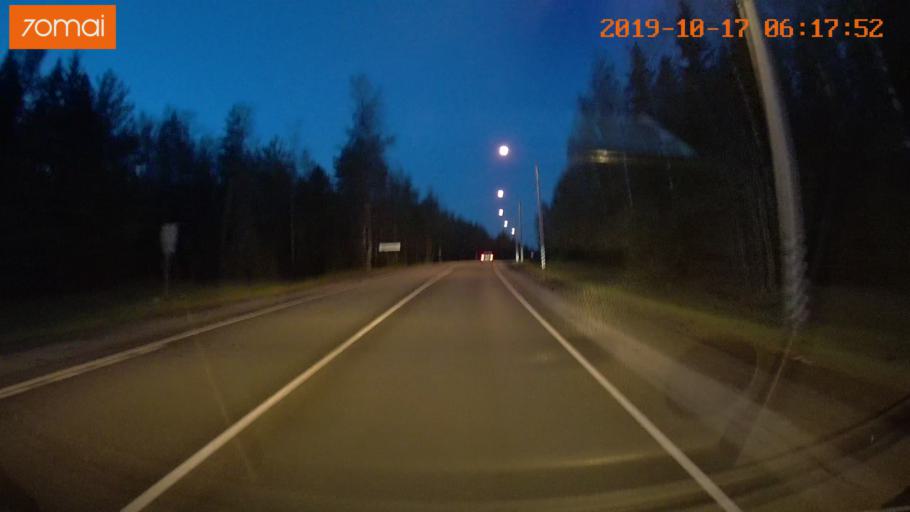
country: RU
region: Ivanovo
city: Lezhnevo
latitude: 56.8474
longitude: 40.9206
